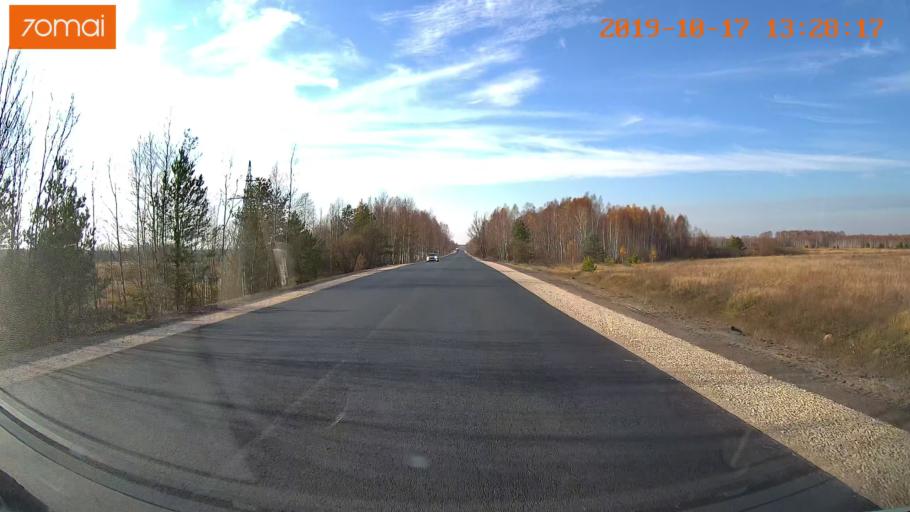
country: RU
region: Vladimir
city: Velikodvorskiy
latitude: 55.1157
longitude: 40.8730
